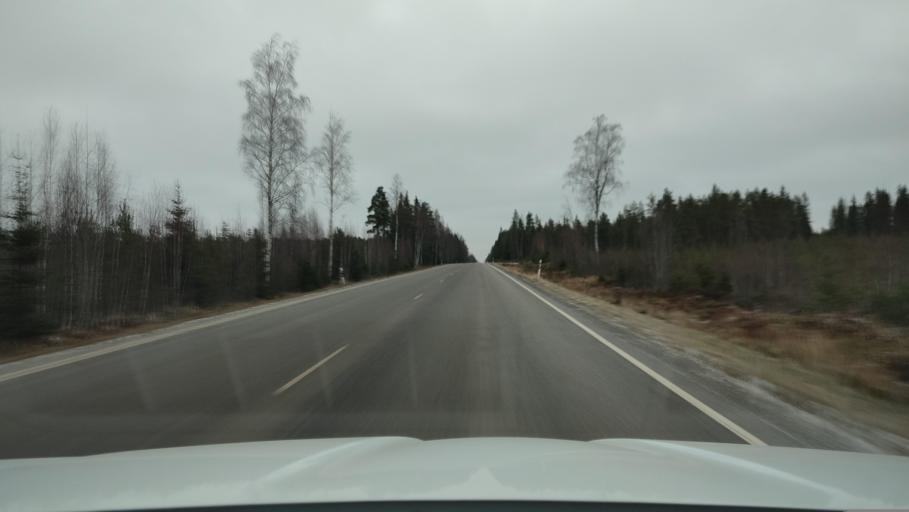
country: FI
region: Ostrobothnia
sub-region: Sydosterbotten
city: Naerpes
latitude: 62.4899
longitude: 21.4438
